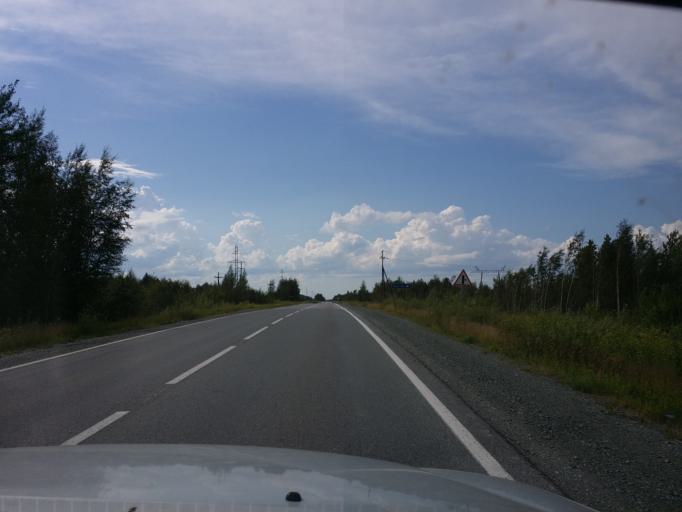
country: RU
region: Khanty-Mansiyskiy Avtonomnyy Okrug
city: Megion
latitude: 61.1029
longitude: 75.9508
